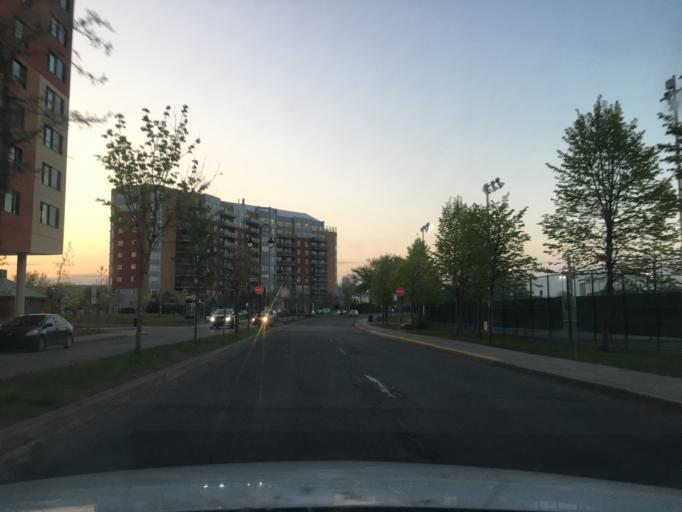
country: CA
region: Quebec
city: Westmount
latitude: 45.4673
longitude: -73.5625
